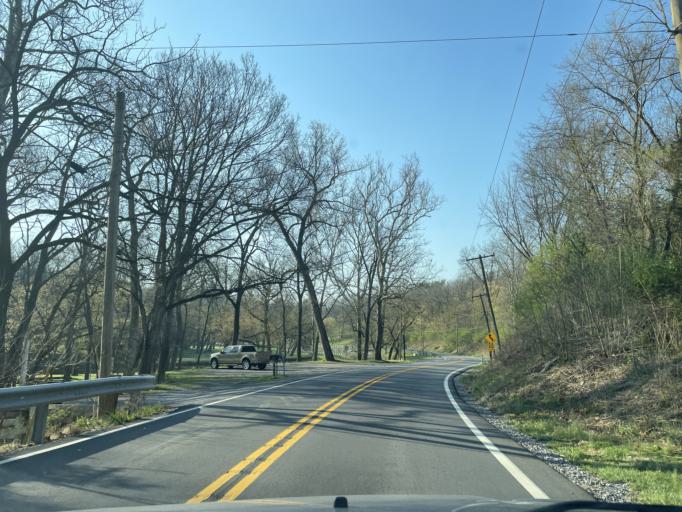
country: US
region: Maryland
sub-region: Washington County
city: Saint James
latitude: 39.5414
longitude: -77.7126
